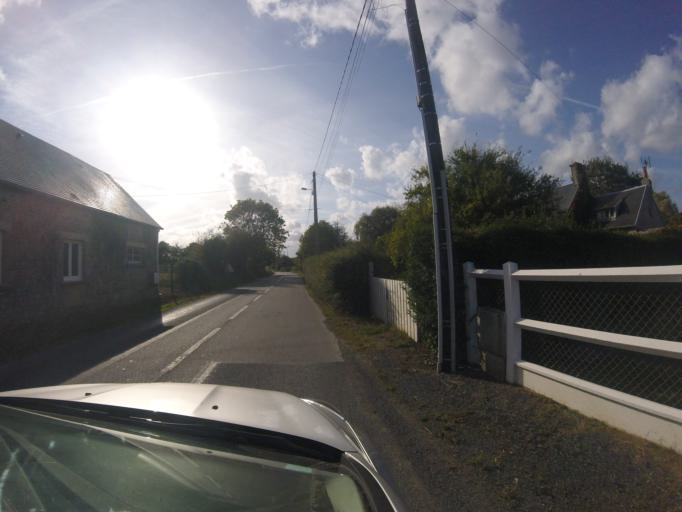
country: FR
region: Lower Normandy
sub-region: Departement du Calvados
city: Port-en-Bessin-Huppain
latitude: 49.3500
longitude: -0.8361
